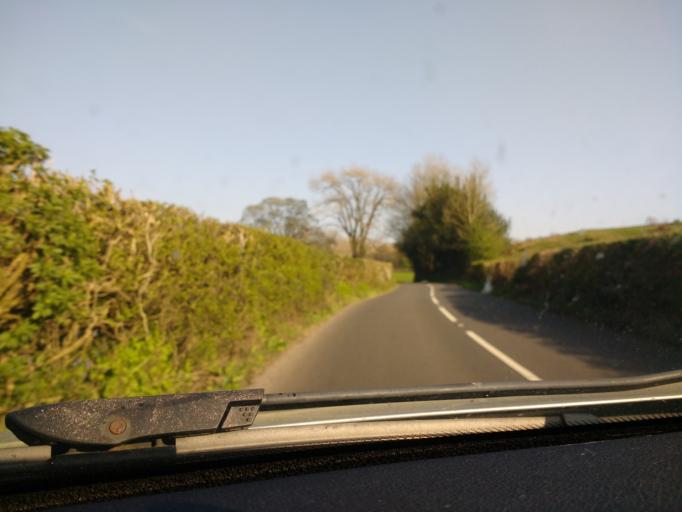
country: GB
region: England
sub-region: Cumbria
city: Sedbergh
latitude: 54.3191
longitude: -2.4897
